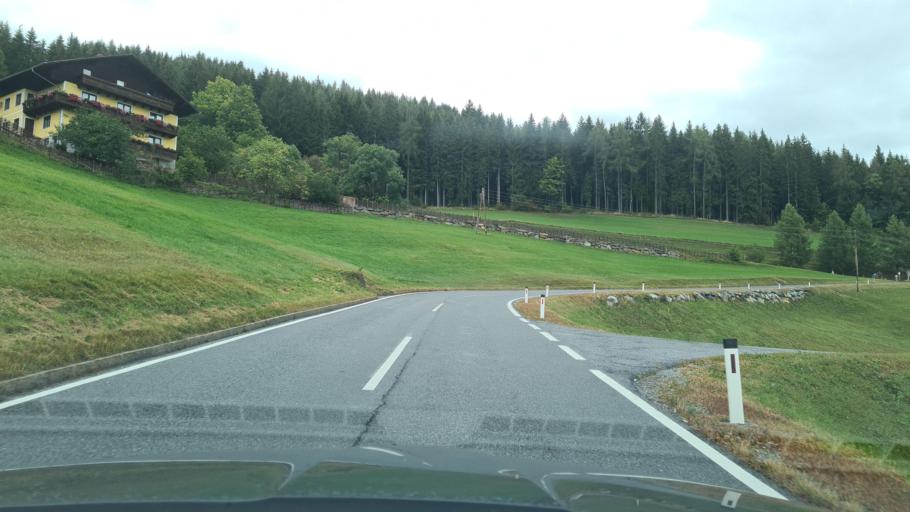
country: AT
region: Styria
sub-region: Politischer Bezirk Weiz
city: Passail
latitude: 47.3062
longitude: 15.4833
